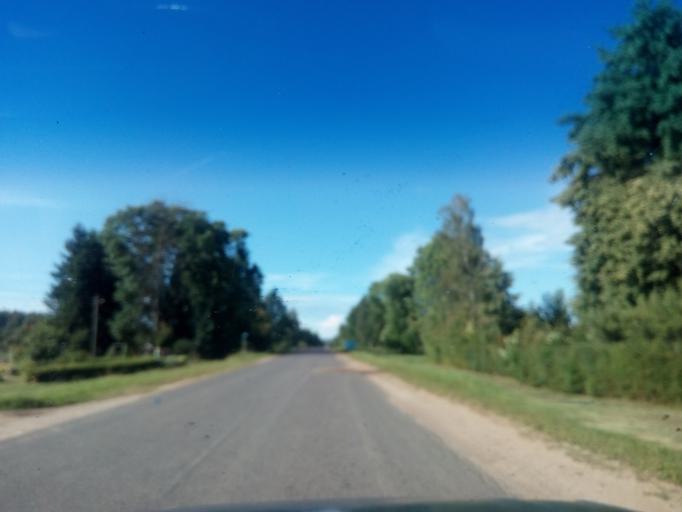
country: BY
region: Vitebsk
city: Dzisna
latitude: 55.6562
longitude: 28.3227
